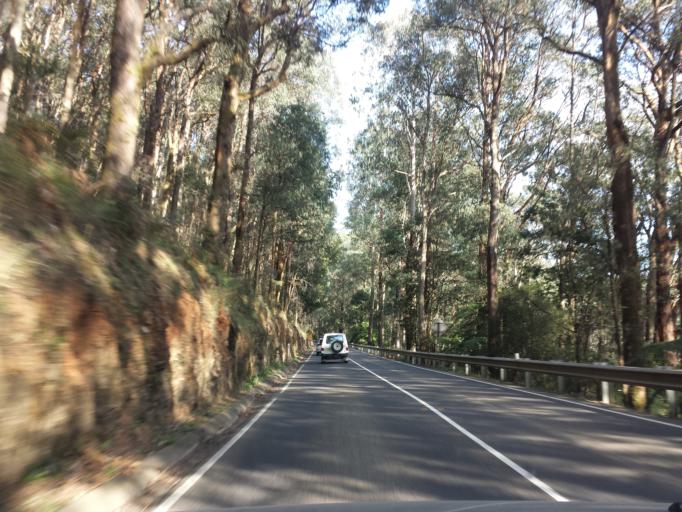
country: AU
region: Victoria
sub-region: Yarra Ranges
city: Healesville
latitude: -37.5867
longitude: 145.6412
